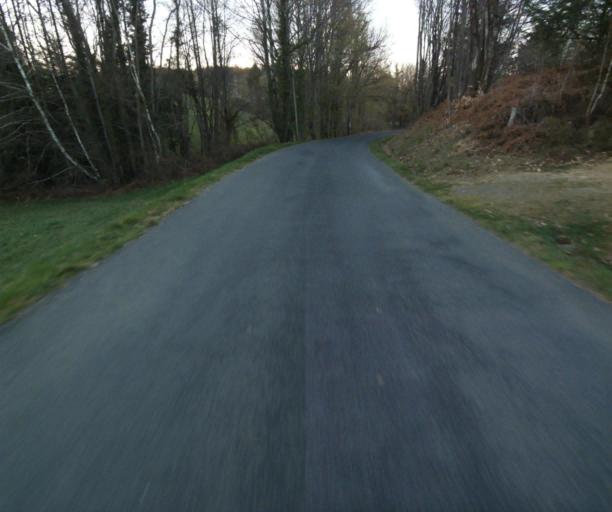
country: FR
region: Limousin
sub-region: Departement de la Correze
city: Sainte-Fereole
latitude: 45.2940
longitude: 1.5715
